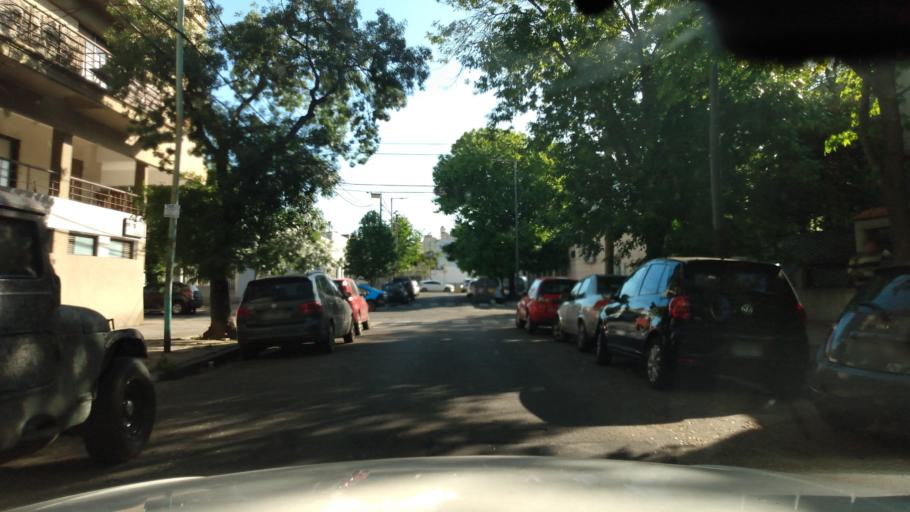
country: AR
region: Buenos Aires
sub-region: Partido de General San Martin
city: General San Martin
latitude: -34.5798
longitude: -58.4935
